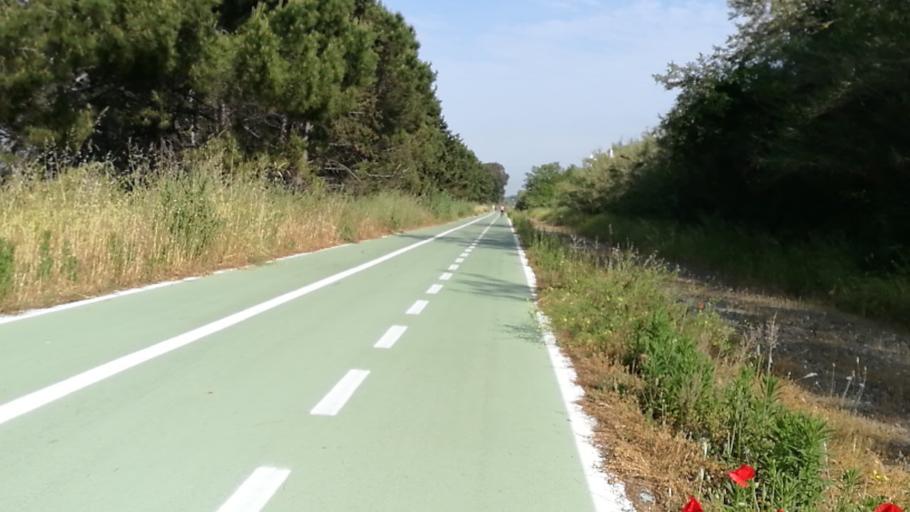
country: IT
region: Abruzzo
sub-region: Provincia di Chieti
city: Casalbordino-Miracoli
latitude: 42.2075
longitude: 14.5972
